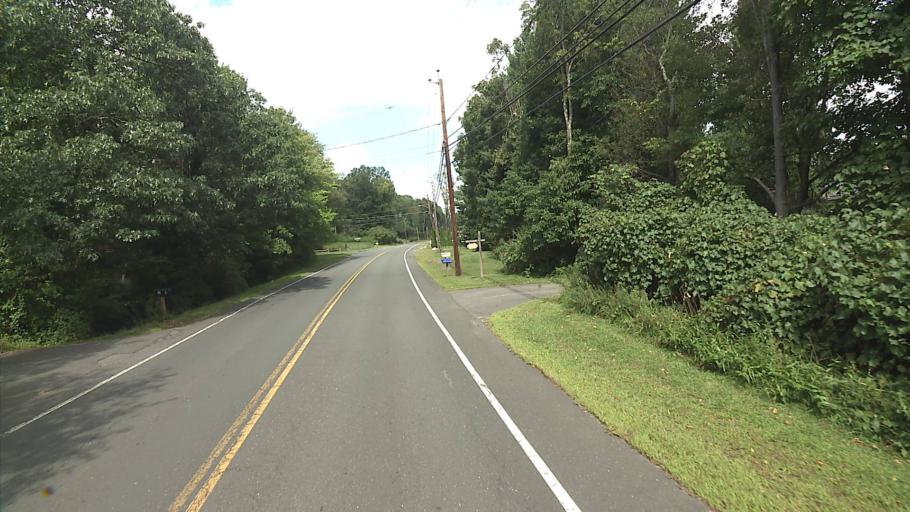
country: US
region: Connecticut
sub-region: Hartford County
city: North Granby
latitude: 42.0039
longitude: -72.8407
